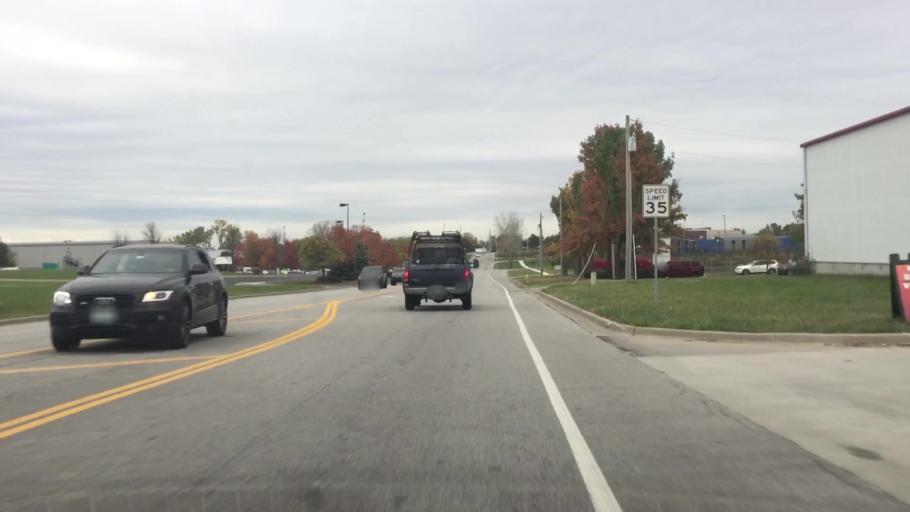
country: US
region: Missouri
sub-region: Jackson County
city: Lees Summit
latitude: 38.9004
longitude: -94.3633
